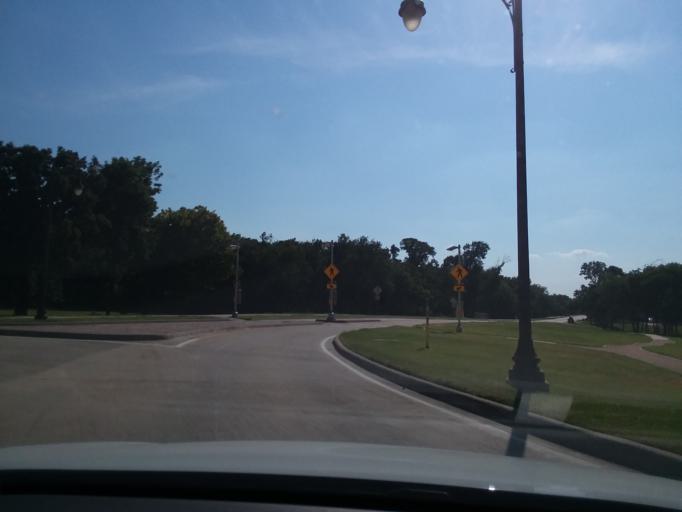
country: US
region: Texas
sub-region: Denton County
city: Double Oak
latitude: 33.0476
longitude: -97.0779
